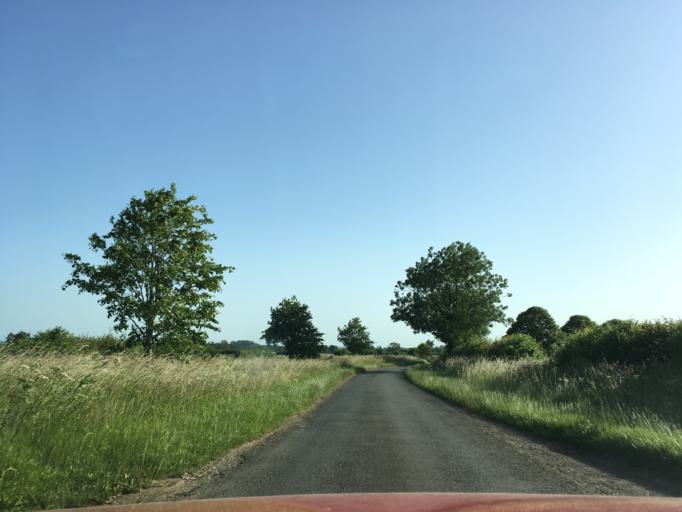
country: GB
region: England
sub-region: Gloucestershire
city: Fairford
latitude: 51.7209
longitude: -1.7627
